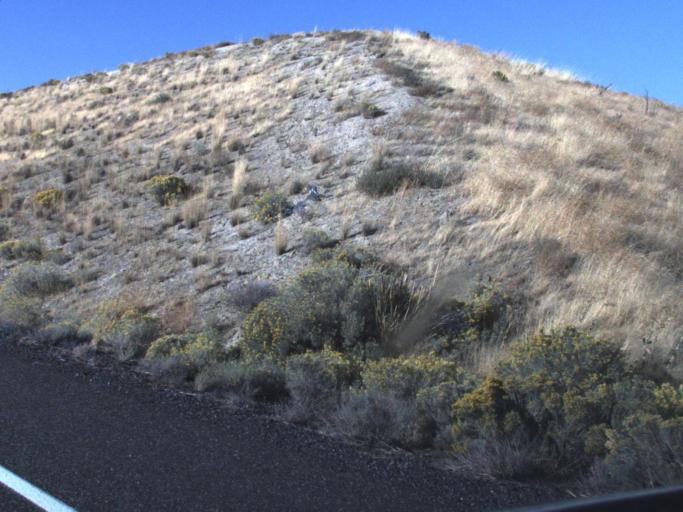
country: US
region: Washington
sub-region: Benton County
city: Highland
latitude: 46.1377
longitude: -119.0994
